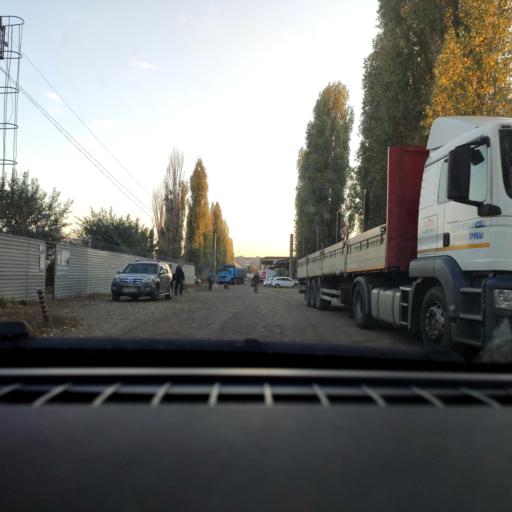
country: RU
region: Voronezj
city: Maslovka
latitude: 51.6402
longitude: 39.2845
